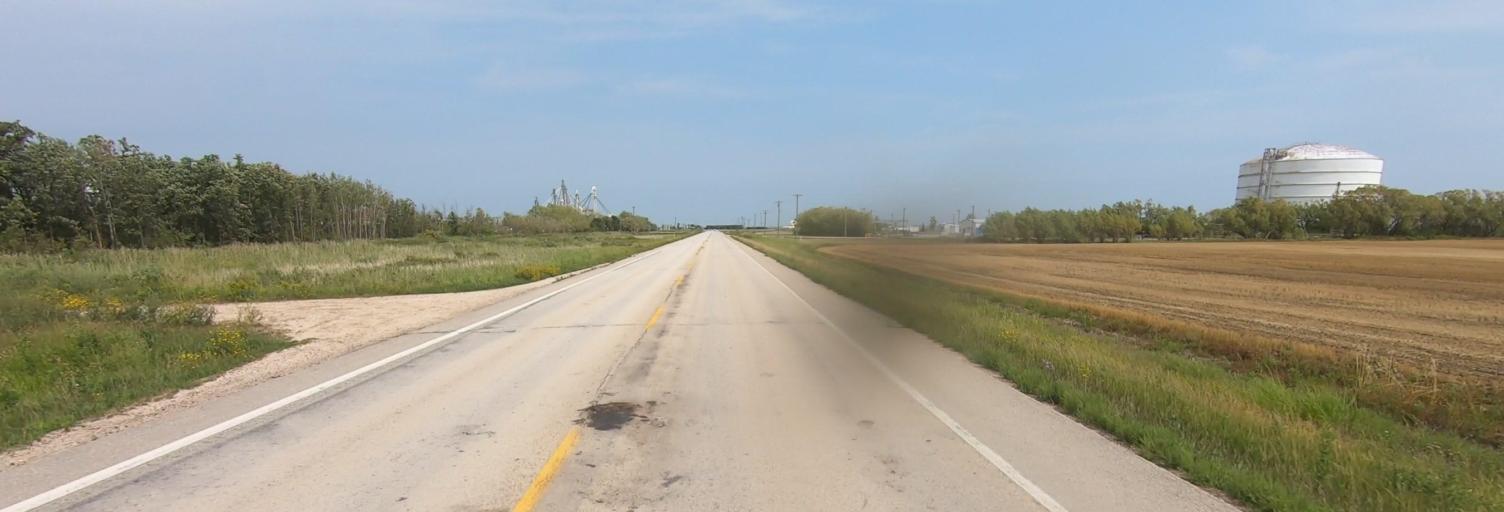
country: CA
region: Manitoba
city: Winnipeg
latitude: 49.7592
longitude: -97.2412
